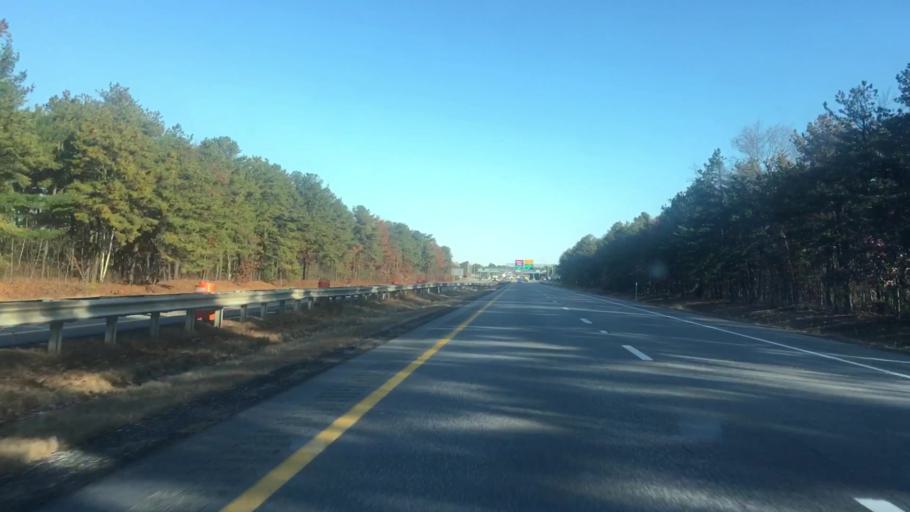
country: US
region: Maine
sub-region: Cumberland County
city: New Gloucester
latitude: 43.9294
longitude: -70.3361
